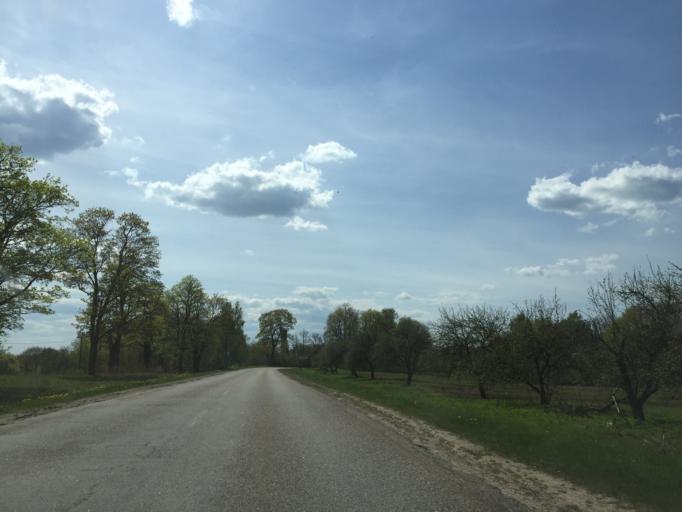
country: LV
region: Limbazu Rajons
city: Limbazi
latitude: 57.3501
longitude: 24.6645
